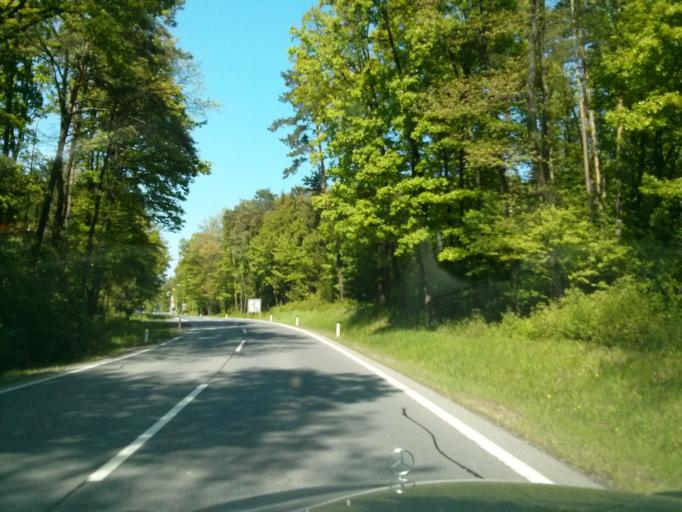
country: AT
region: Burgenland
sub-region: Politischer Bezirk Oberwart
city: Bad Tatzmannsdorf
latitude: 47.3320
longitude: 16.2205
